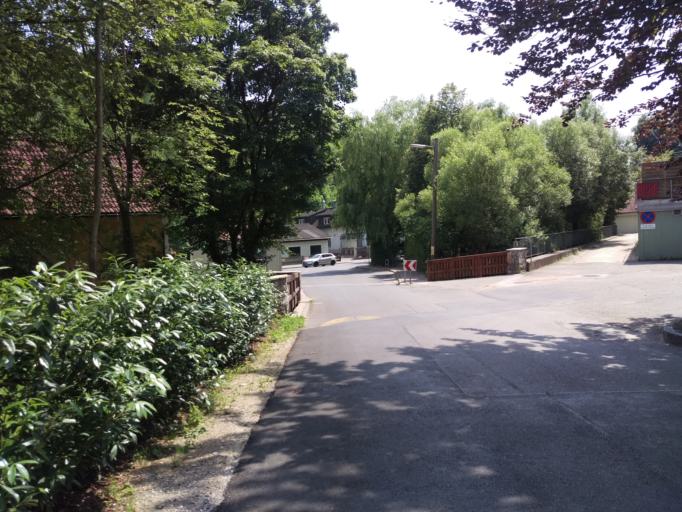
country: AT
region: Styria
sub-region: Graz Stadt
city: Mariatrost
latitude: 47.1083
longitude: 15.4897
